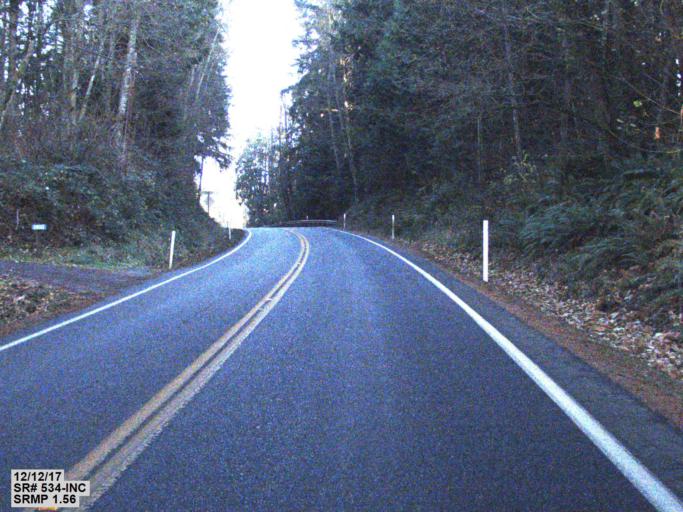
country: US
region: Washington
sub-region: Skagit County
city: Big Lake
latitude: 48.3380
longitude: -122.3022
